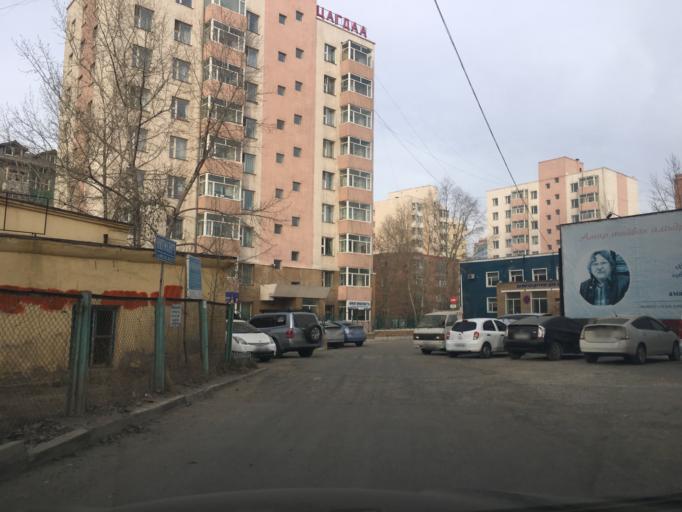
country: MN
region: Ulaanbaatar
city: Ulaanbaatar
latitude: 47.9156
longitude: 106.8825
